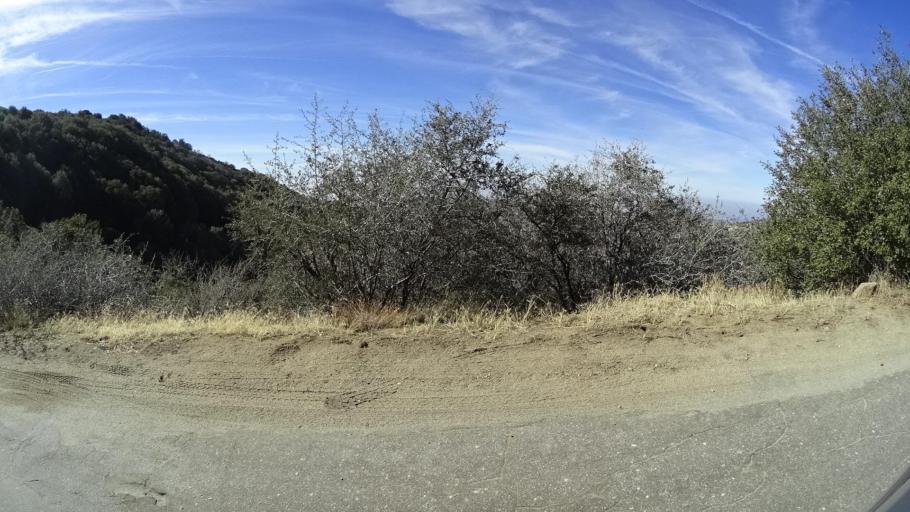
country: US
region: California
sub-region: Kern County
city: Bodfish
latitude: 35.4648
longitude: -118.6482
